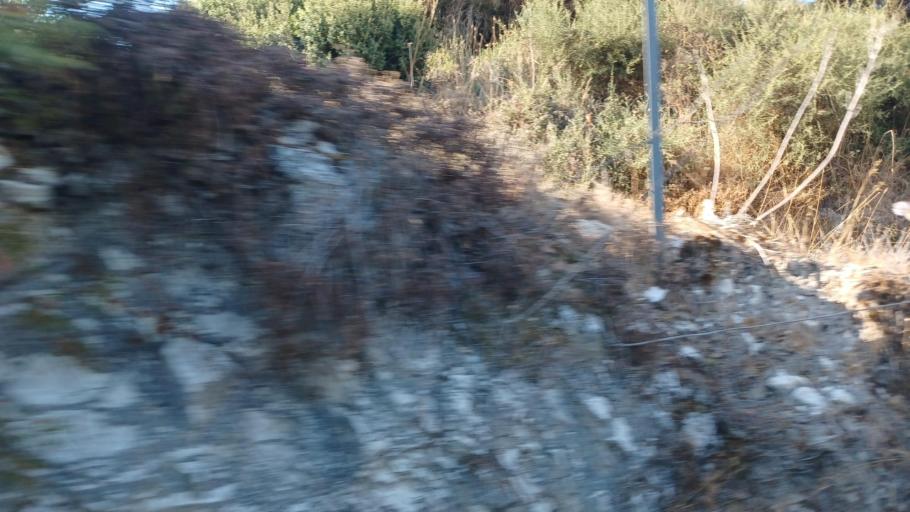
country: CY
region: Pafos
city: Mesogi
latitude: 34.8826
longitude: 32.5205
